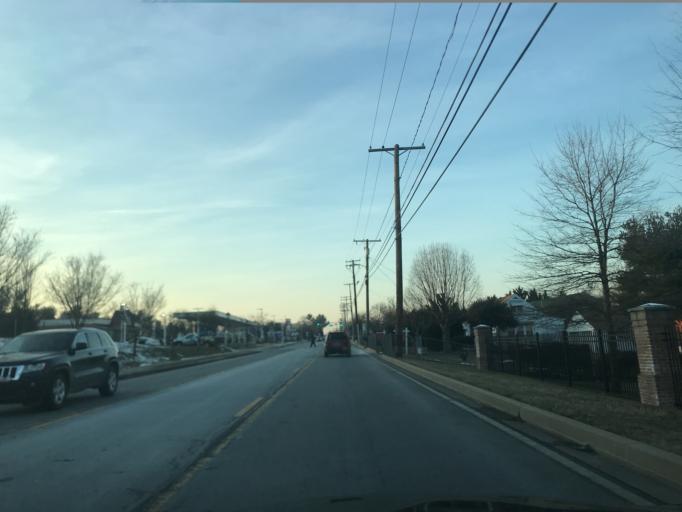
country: US
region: Maryland
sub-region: Harford County
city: Edgewood
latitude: 39.4253
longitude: -76.2974
